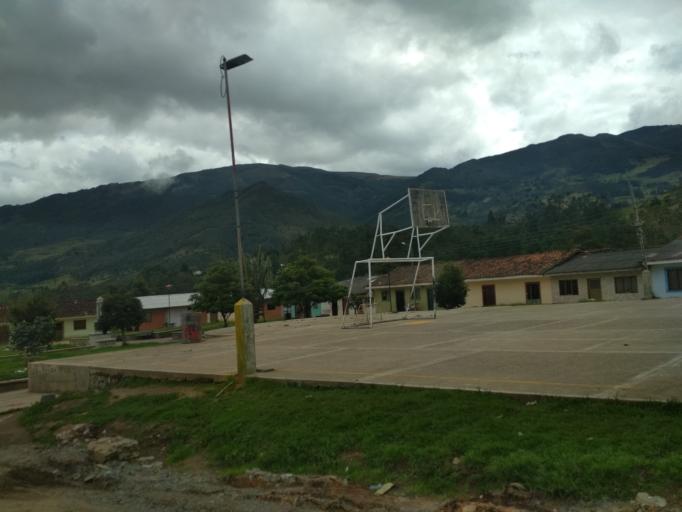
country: CO
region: Cauca
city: Jambalo
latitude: 2.7130
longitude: -76.3247
